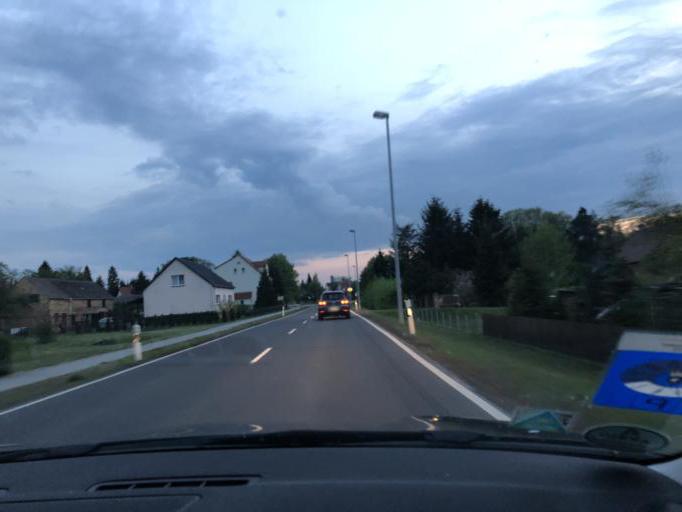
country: DE
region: Saxony
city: Krauschwitz
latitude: 51.5194
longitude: 14.7213
